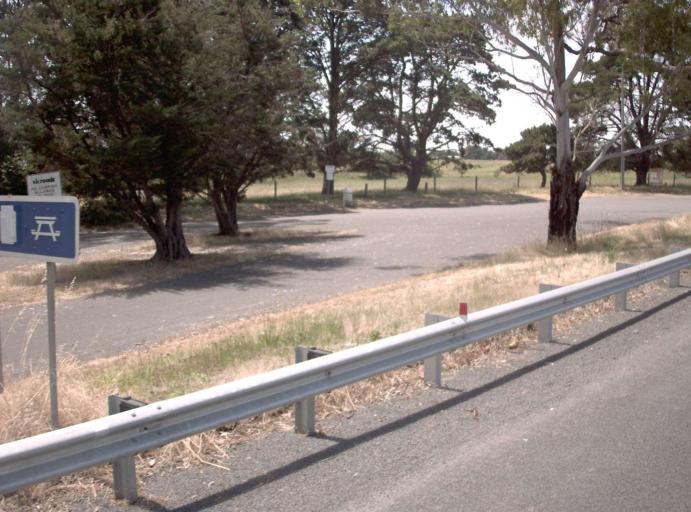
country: AU
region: Victoria
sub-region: Latrobe
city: Traralgon
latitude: -38.2113
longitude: 146.4864
